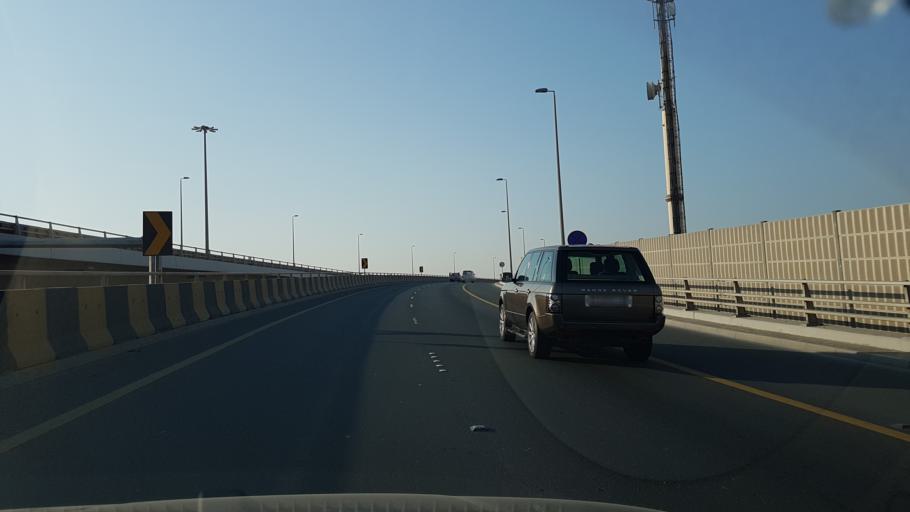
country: BH
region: Northern
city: Madinat `Isa
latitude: 26.1682
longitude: 50.5447
